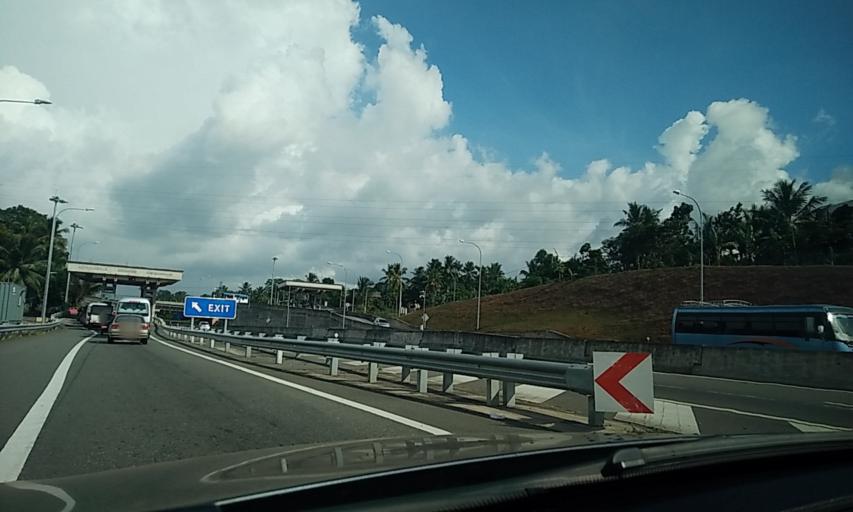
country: LK
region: Western
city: Mulleriyawa
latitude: 6.9226
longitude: 79.9799
